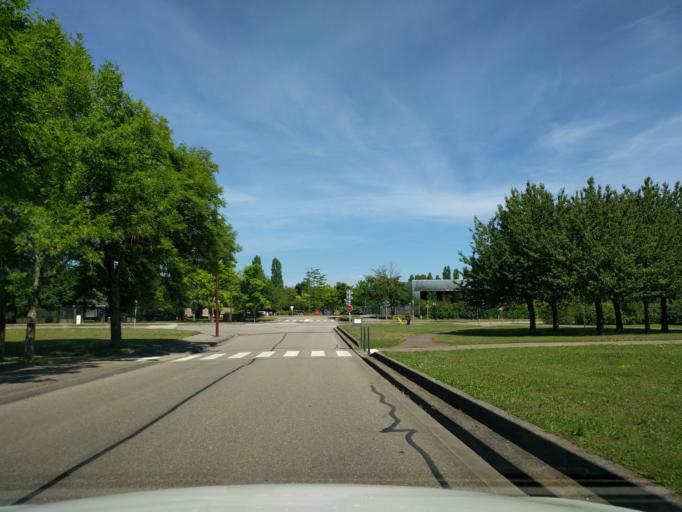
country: FR
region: Lorraine
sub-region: Departement de la Moselle
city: Saint-Julien-les-Metz
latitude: 49.1042
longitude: 6.2151
